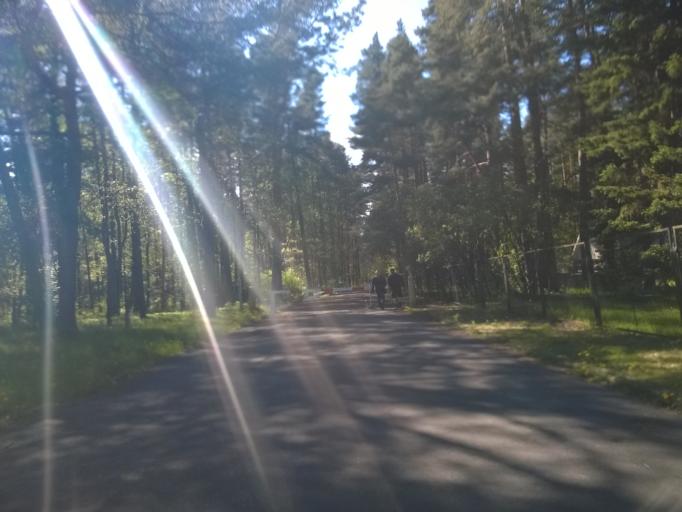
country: LV
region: Jurmala
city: Jurmala
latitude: 56.9592
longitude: 23.6448
